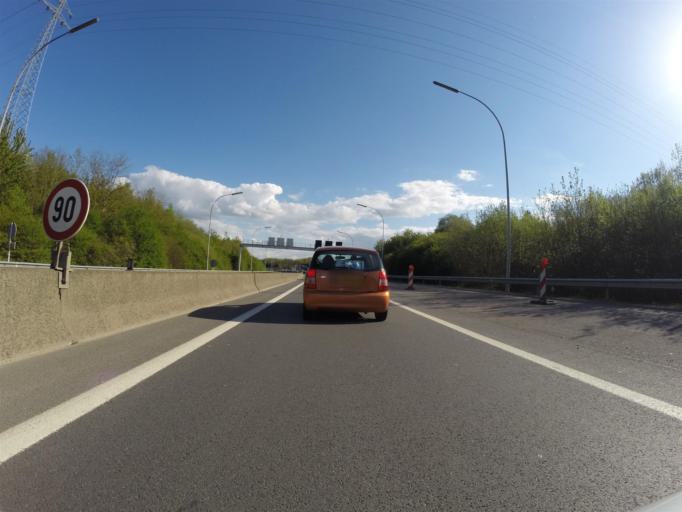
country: LU
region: Luxembourg
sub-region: Canton de Luxembourg
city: Hesperange
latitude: 49.5747
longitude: 6.1244
